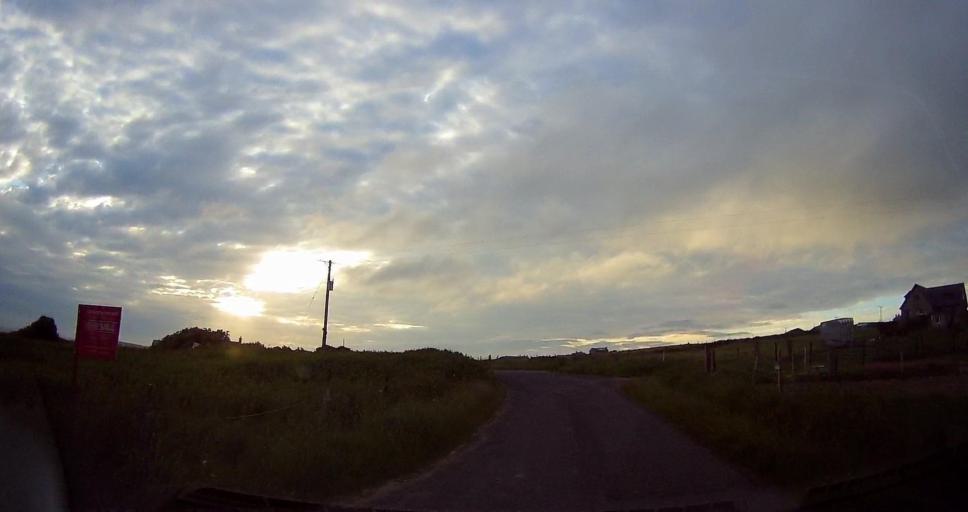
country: GB
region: Scotland
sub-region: Orkney Islands
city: Stromness
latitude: 59.1242
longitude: -3.2791
